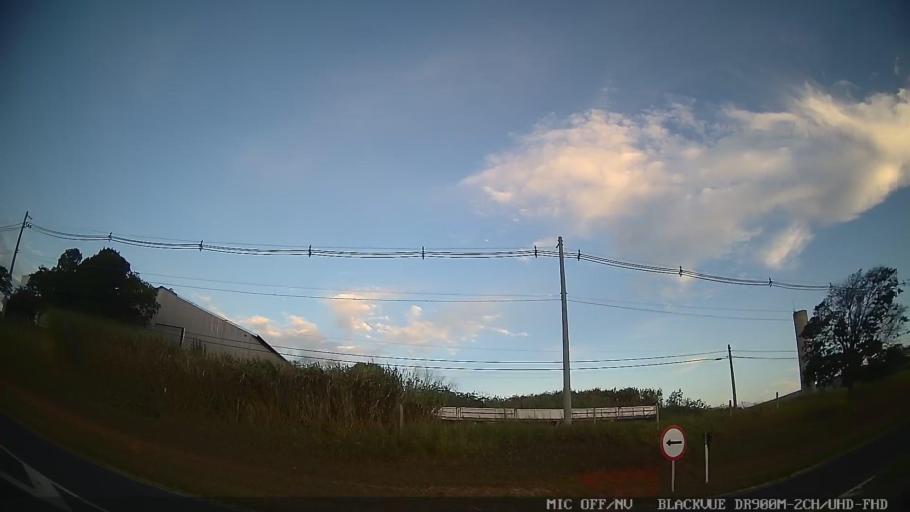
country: BR
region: Sao Paulo
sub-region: Indaiatuba
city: Indaiatuba
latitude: -23.1311
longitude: -47.2342
